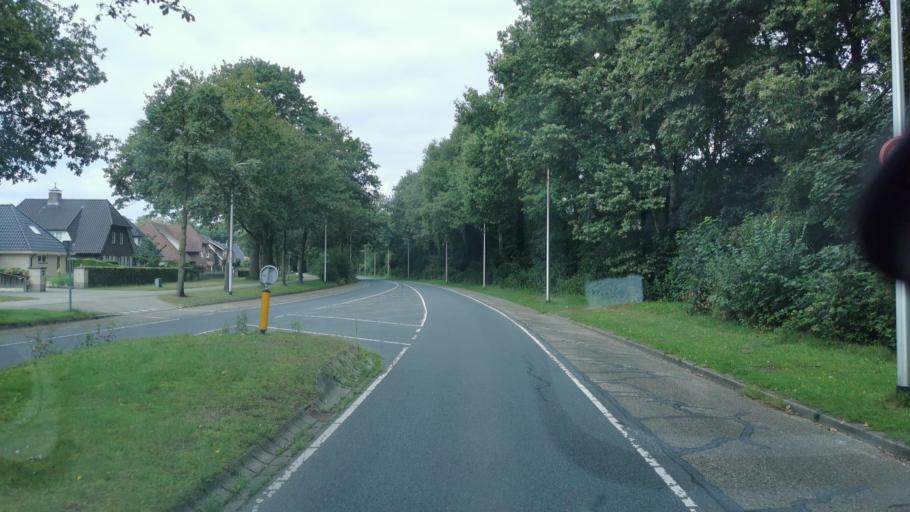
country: NL
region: Overijssel
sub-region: Gemeente Oldenzaal
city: Oldenzaal
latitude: 52.3108
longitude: 6.9010
